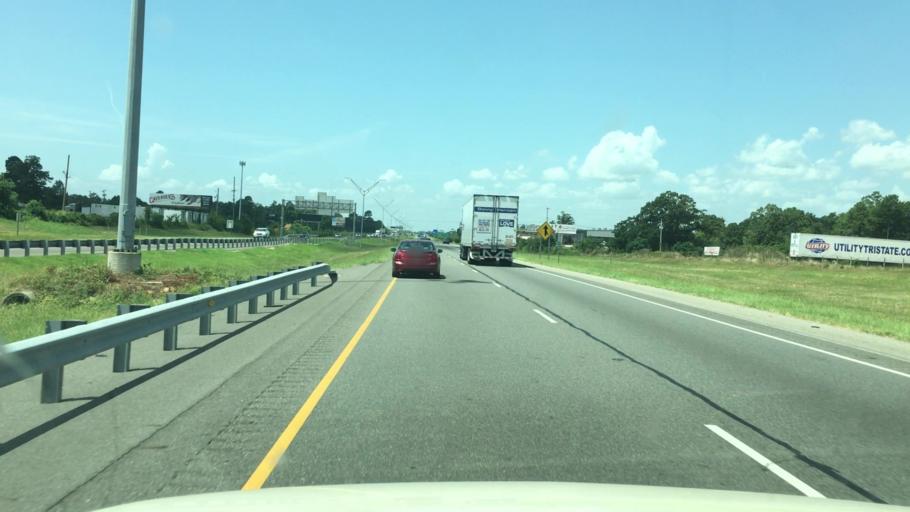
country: US
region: Arkansas
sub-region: Miller County
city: Texarkana
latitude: 33.4757
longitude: -94.0087
